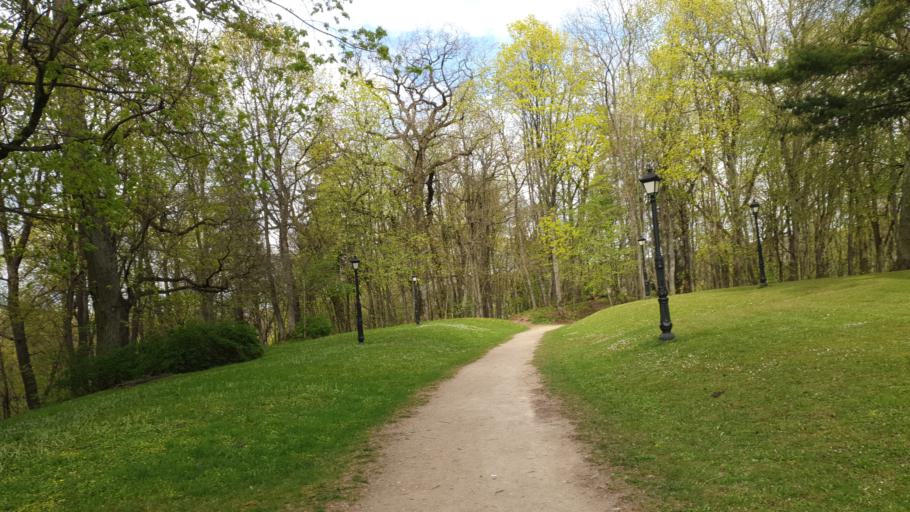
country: LT
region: Kauno apskritis
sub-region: Kauno rajonas
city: Akademija (Kaunas)
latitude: 54.9442
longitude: 23.7839
